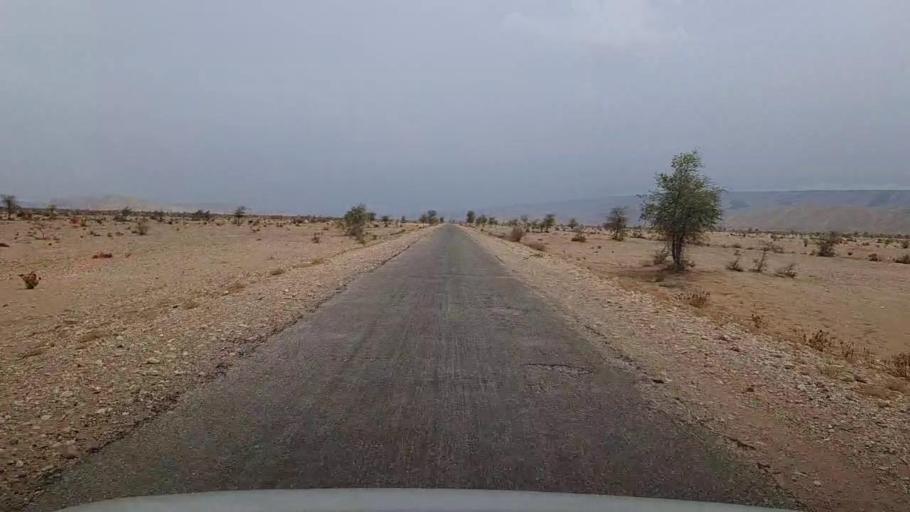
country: PK
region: Sindh
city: Sehwan
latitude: 26.2658
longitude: 67.7234
